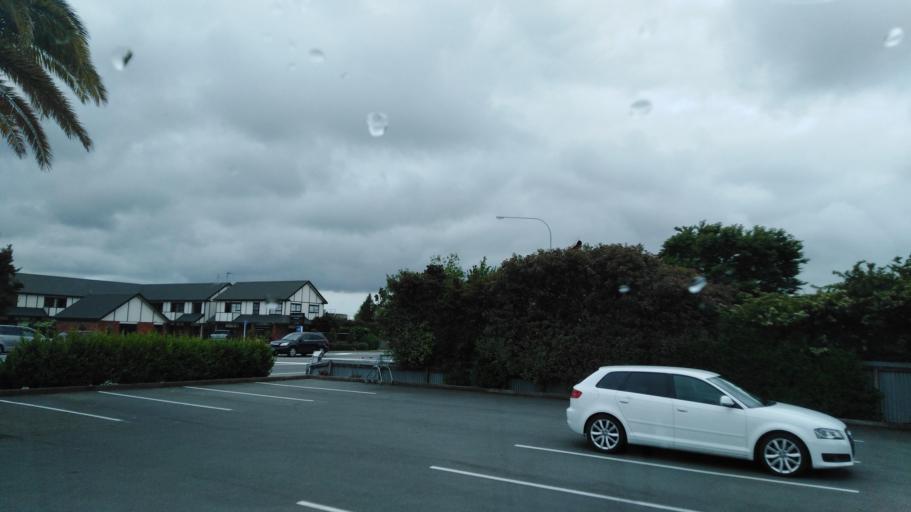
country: NZ
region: Marlborough
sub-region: Marlborough District
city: Blenheim
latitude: -41.5094
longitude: 173.9360
